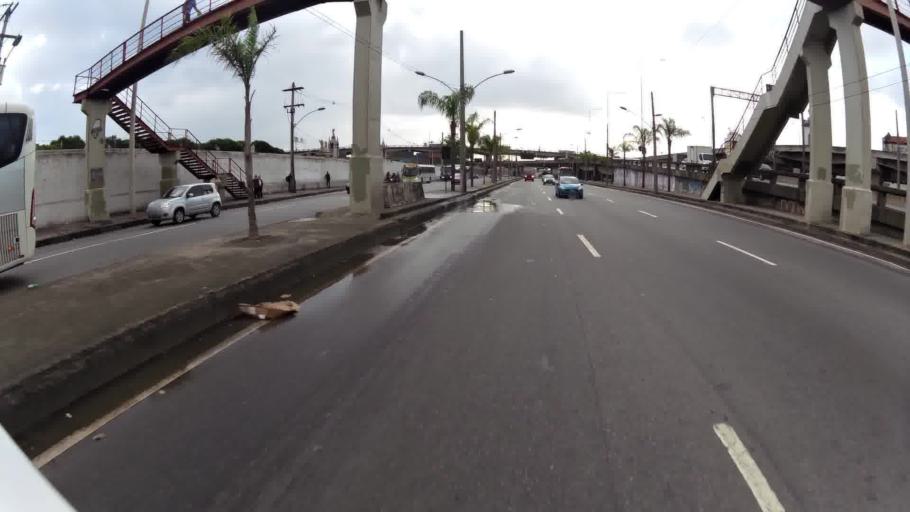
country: BR
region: Rio de Janeiro
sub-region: Rio De Janeiro
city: Rio de Janeiro
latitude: -22.8888
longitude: -43.2206
